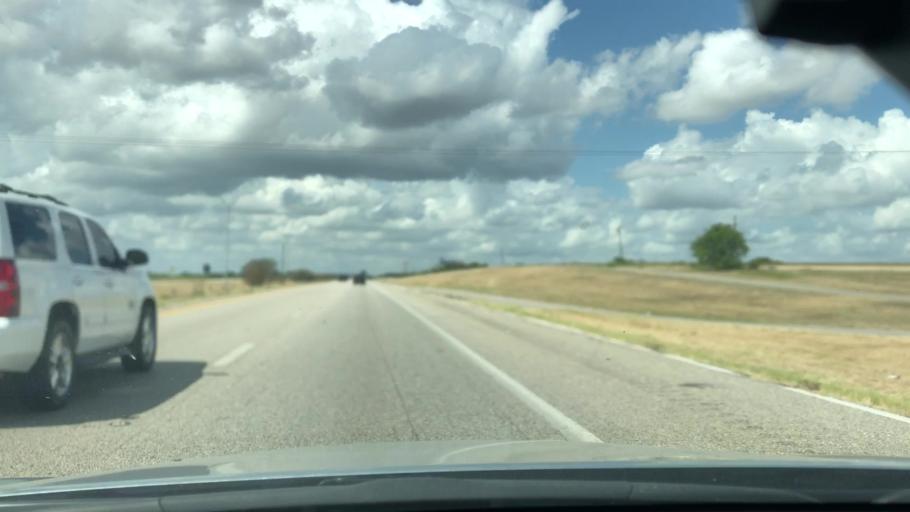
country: US
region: Texas
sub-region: Guadalupe County
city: McQueeney
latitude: 29.5600
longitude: -98.0334
